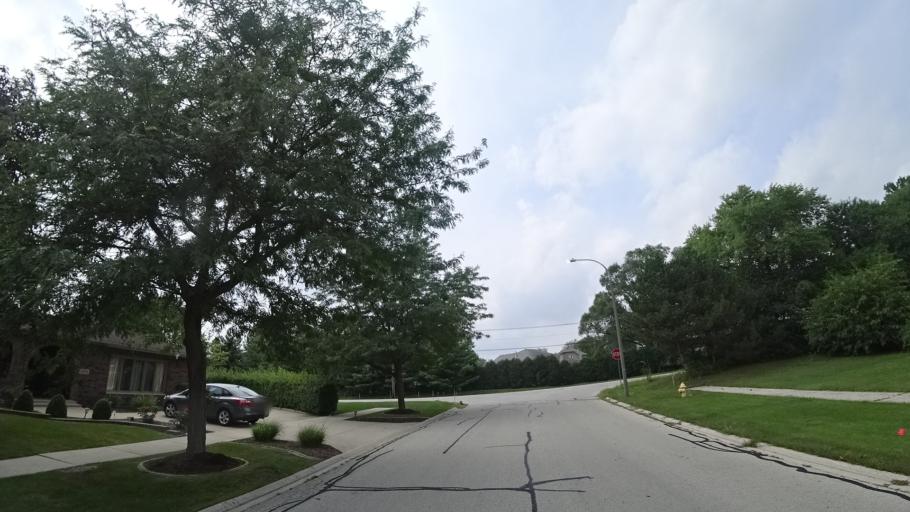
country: US
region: Illinois
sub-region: Will County
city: Goodings Grove
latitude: 41.6255
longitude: -87.9109
